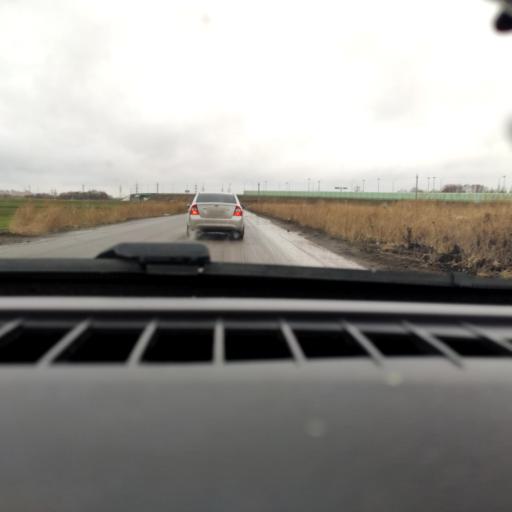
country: RU
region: Voronezj
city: Novaya Usman'
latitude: 51.6483
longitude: 39.3139
